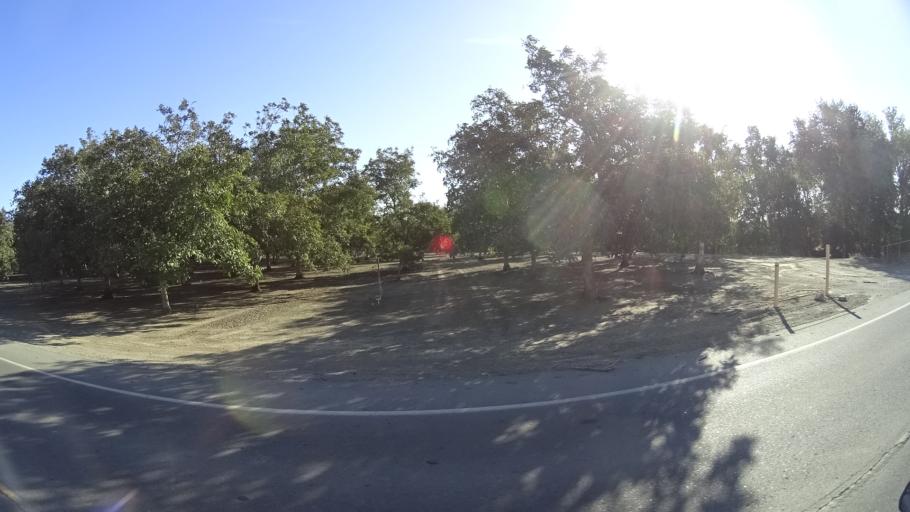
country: US
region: California
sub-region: Yolo County
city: Davis
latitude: 38.5956
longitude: -121.7856
